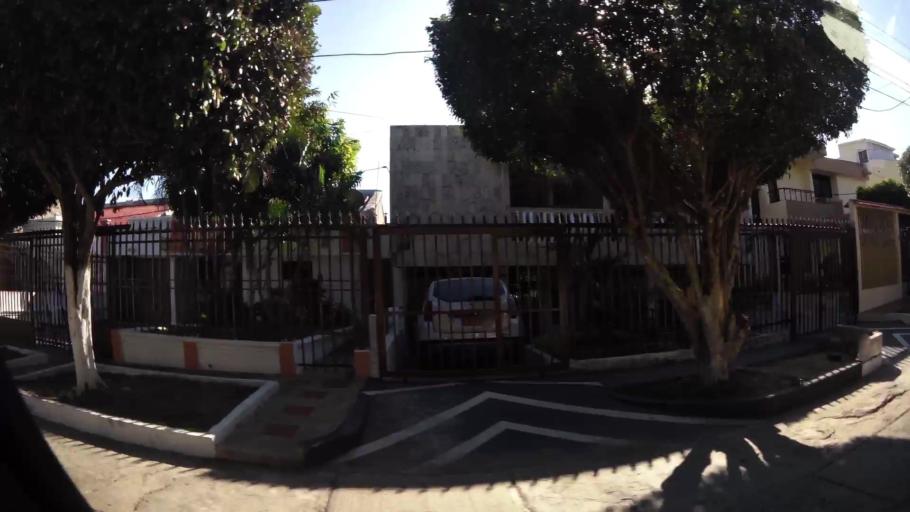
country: CO
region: Atlantico
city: Barranquilla
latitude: 10.9918
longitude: -74.8269
